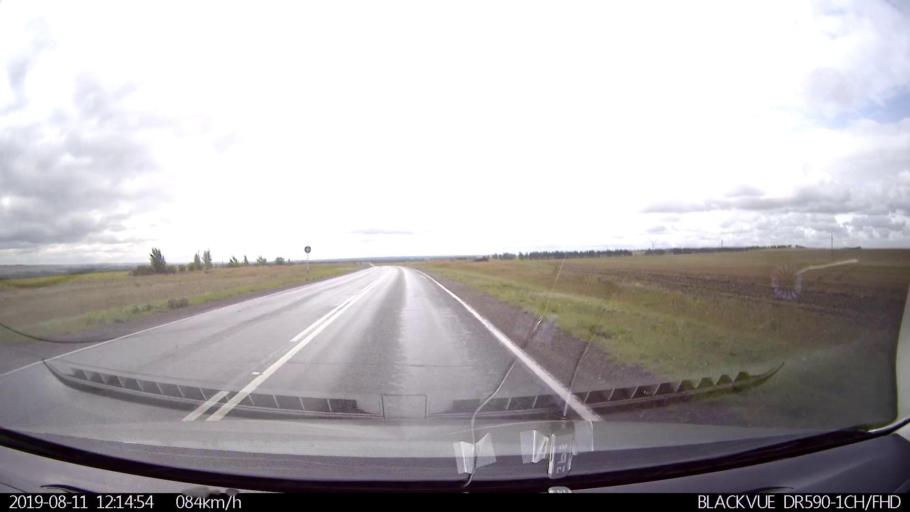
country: RU
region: Ulyanovsk
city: Ignatovka
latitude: 53.9475
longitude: 47.9739
